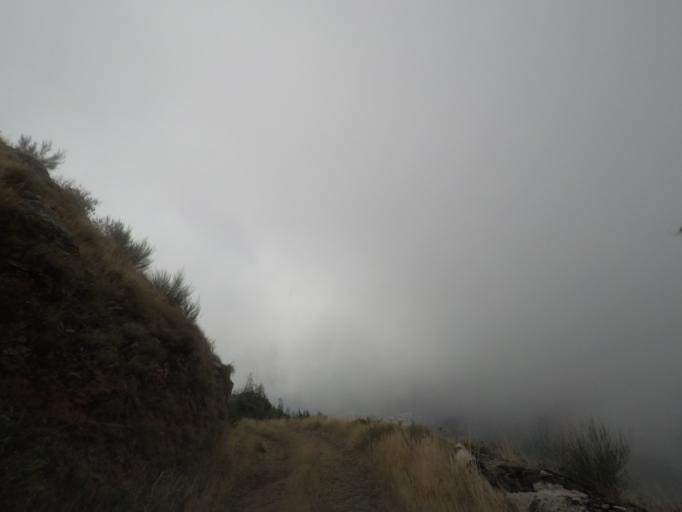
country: PT
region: Madeira
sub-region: Funchal
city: Nossa Senhora do Monte
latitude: 32.7004
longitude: -16.9157
